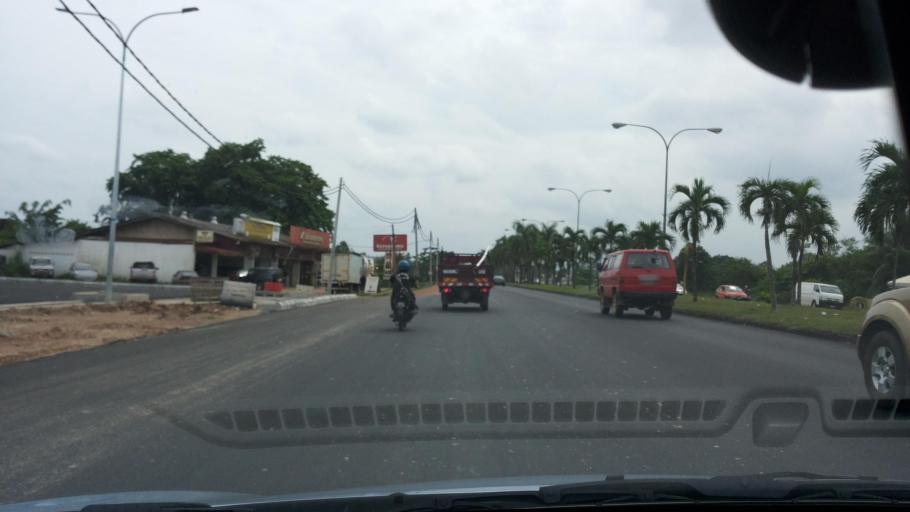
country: MY
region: Pahang
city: Kuantan
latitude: 3.7696
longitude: 103.2450
